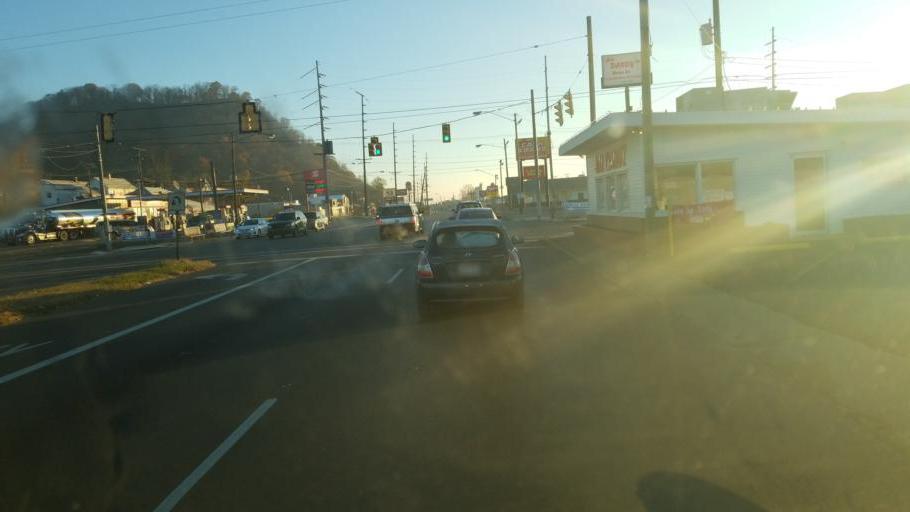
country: US
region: Kentucky
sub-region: Greenup County
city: South Shore
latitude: 38.7393
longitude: -82.9692
